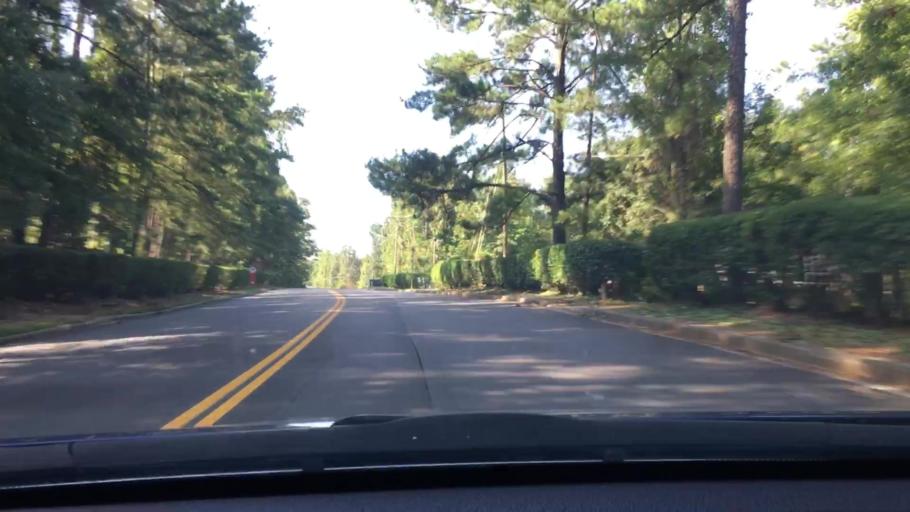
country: US
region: South Carolina
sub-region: Lexington County
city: Seven Oaks
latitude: 34.0785
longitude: -81.1403
